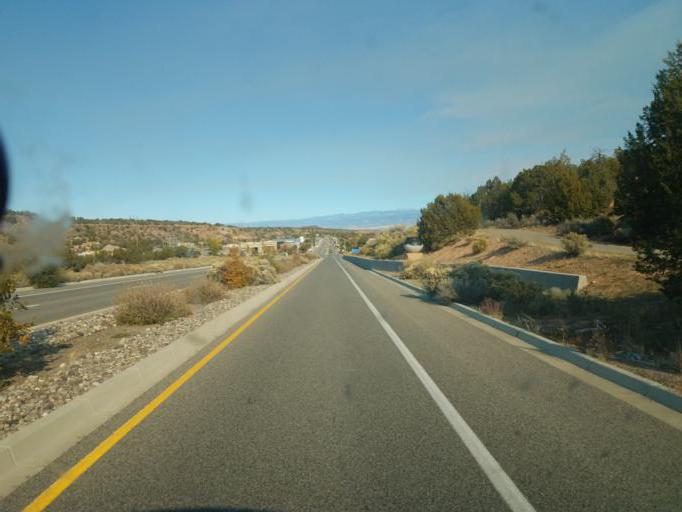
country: US
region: New Mexico
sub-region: Los Alamos County
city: White Rock
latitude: 35.8256
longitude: -106.2151
